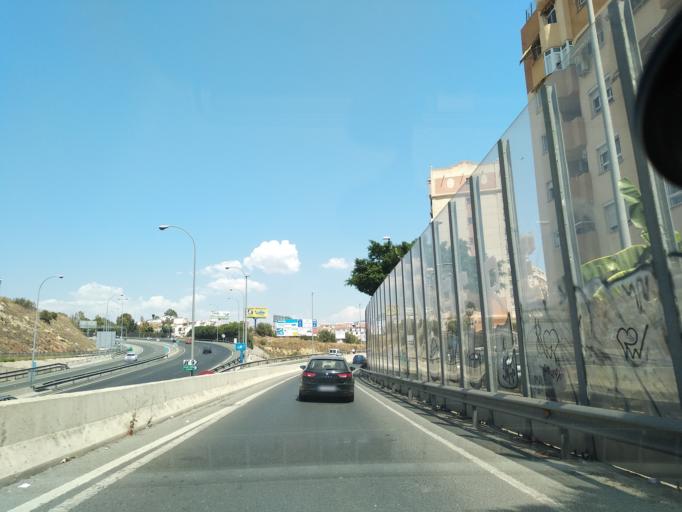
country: ES
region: Andalusia
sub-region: Provincia de Malaga
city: Malaga
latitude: 36.7245
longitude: -4.4543
